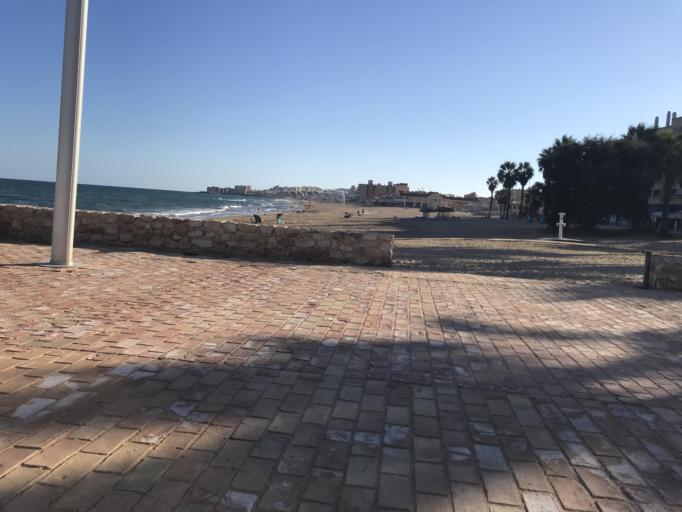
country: ES
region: Valencia
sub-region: Provincia de Alicante
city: Torrevieja
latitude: 38.0262
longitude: -0.6529
